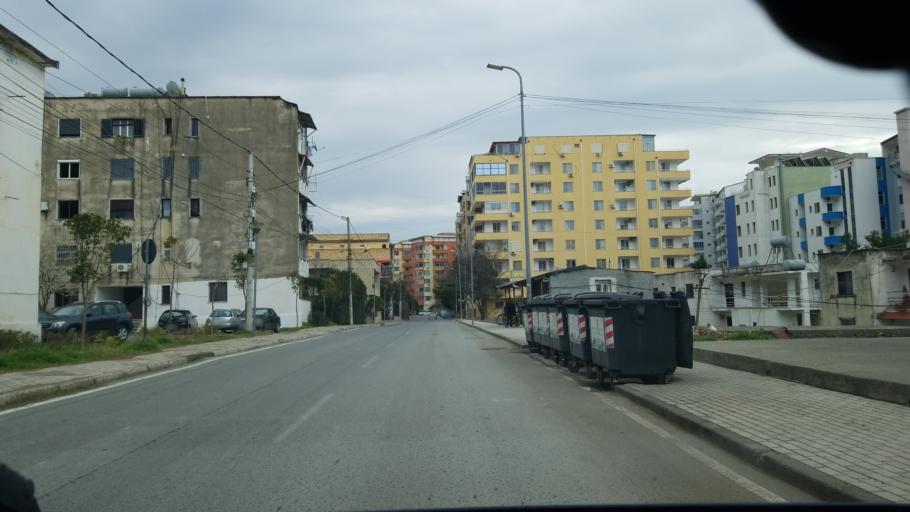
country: AL
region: Lezhe
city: Shengjin
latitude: 41.8113
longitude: 19.5968
